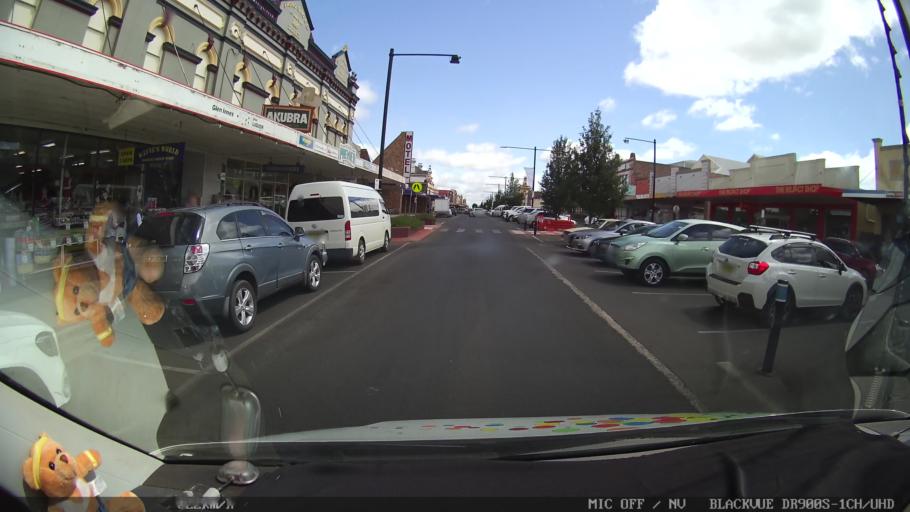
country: AU
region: New South Wales
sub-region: Glen Innes Severn
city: Glen Innes
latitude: -29.7404
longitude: 151.7352
